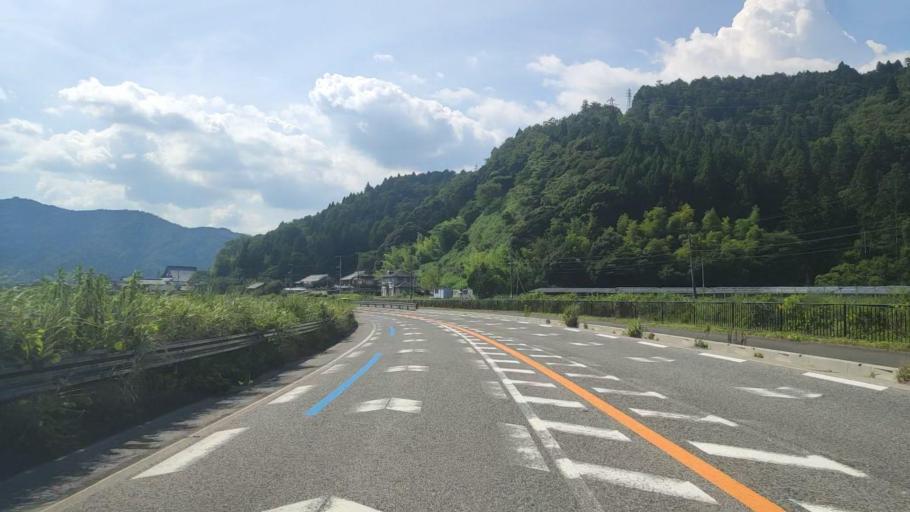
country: JP
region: Shiga Prefecture
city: Nagahama
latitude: 35.5143
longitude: 136.1716
